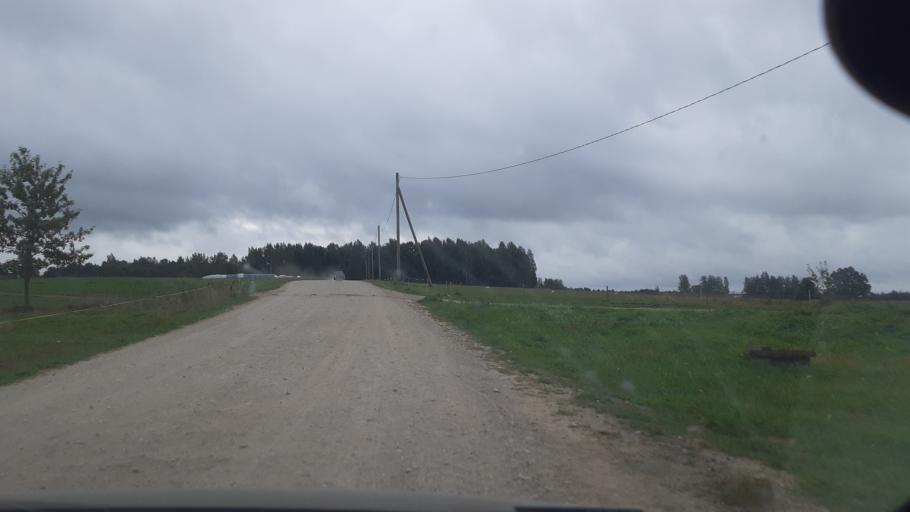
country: LV
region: Alsunga
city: Alsunga
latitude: 56.8977
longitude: 21.6885
